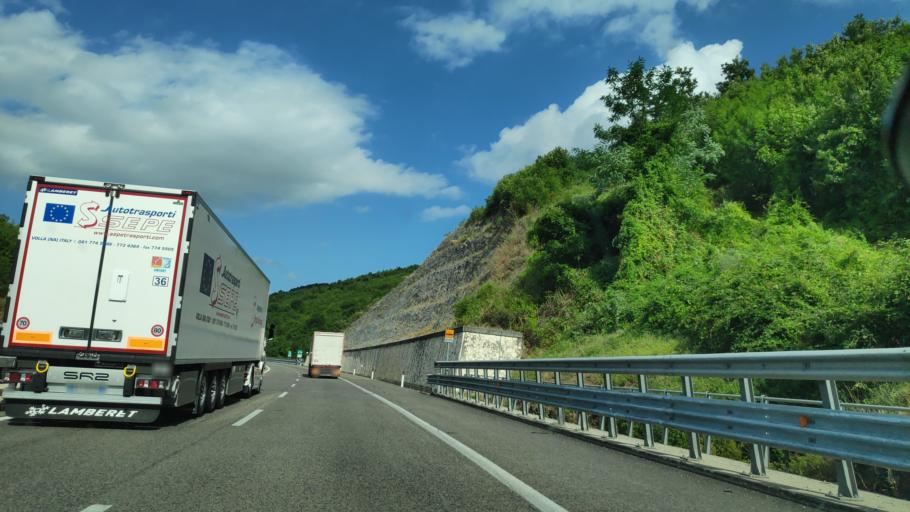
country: IT
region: Campania
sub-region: Provincia di Salerno
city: Pertosa
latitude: 40.5311
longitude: 15.4503
